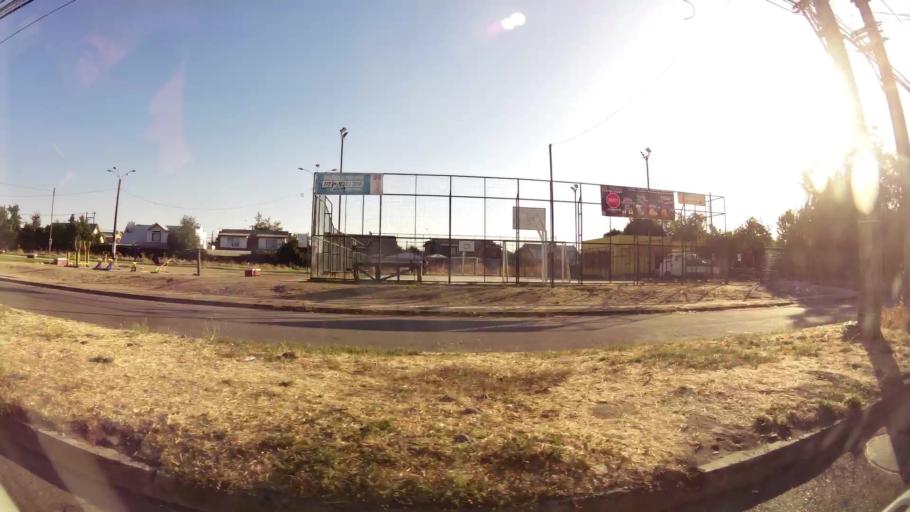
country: CL
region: Maule
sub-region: Provincia de Talca
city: Talca
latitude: -35.4460
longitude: -71.6828
